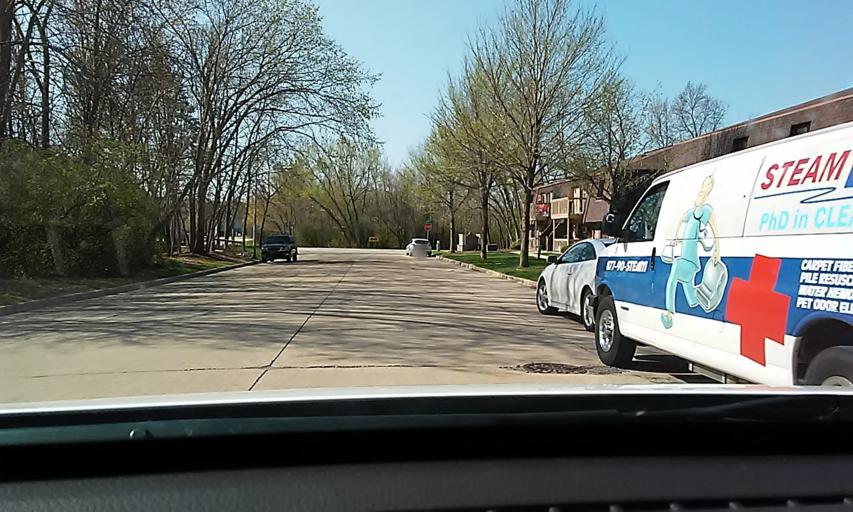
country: US
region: Wisconsin
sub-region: Milwaukee County
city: Hales Corners
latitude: 42.9816
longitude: -88.0536
